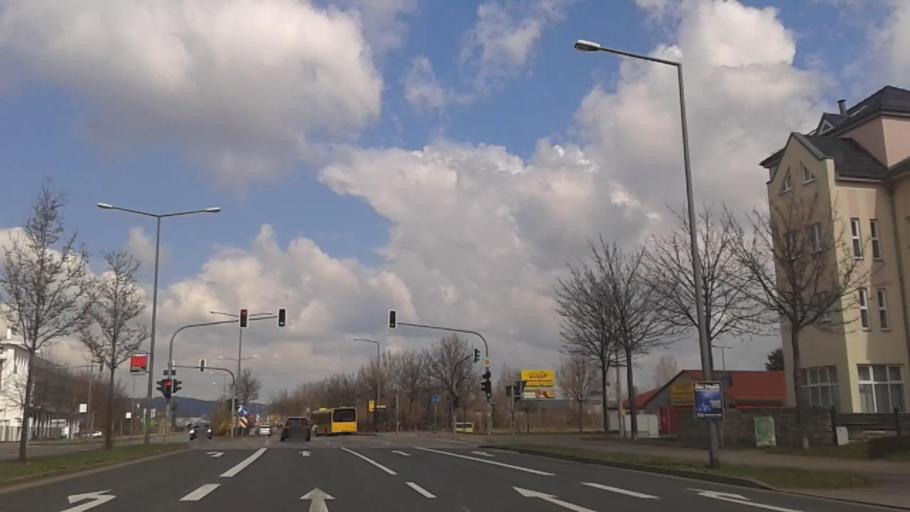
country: DE
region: Saxony
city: Radebeul
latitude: 51.0733
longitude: 13.6902
